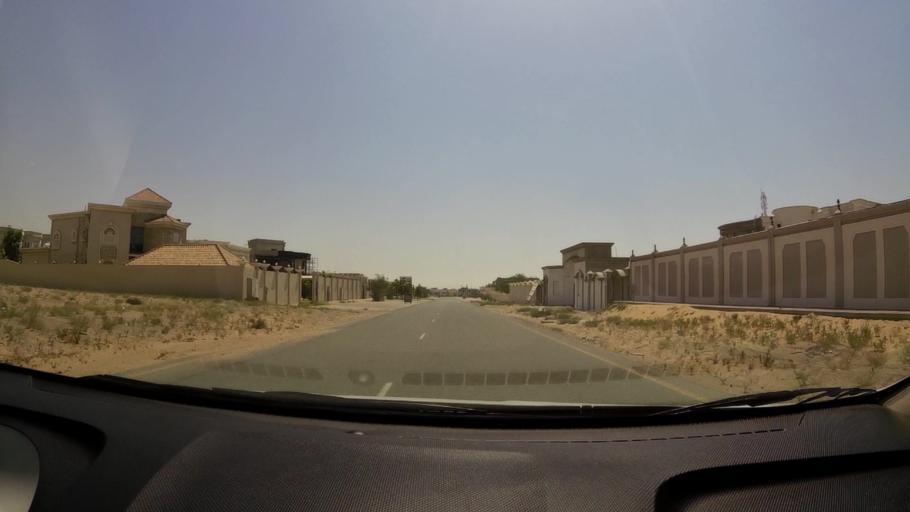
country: AE
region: Umm al Qaywayn
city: Umm al Qaywayn
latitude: 25.4942
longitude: 55.5855
